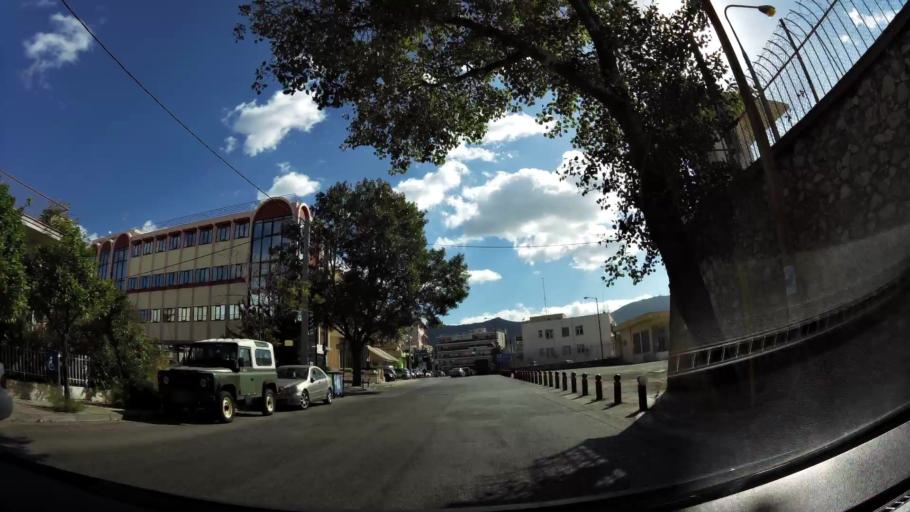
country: GR
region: Attica
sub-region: Nomarchia Athinas
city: Neo Psychiko
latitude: 38.0016
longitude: 23.7860
